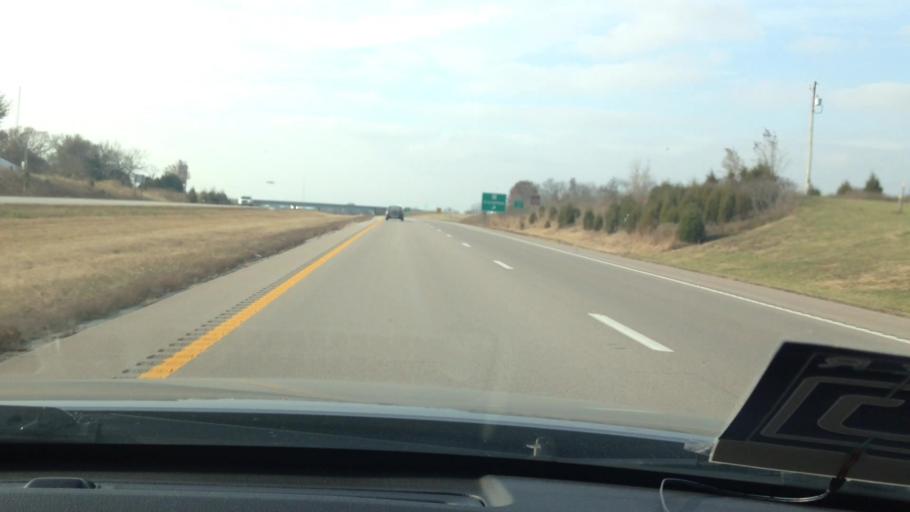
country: US
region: Missouri
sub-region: Cass County
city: Garden City
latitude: 38.4981
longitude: -94.0652
